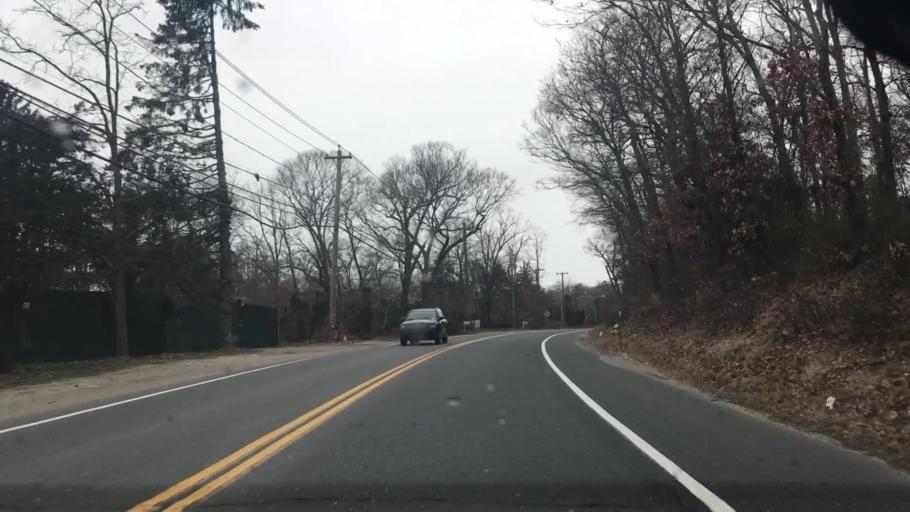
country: US
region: New York
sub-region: Suffolk County
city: Yaphank
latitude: 40.8491
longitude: -72.9368
